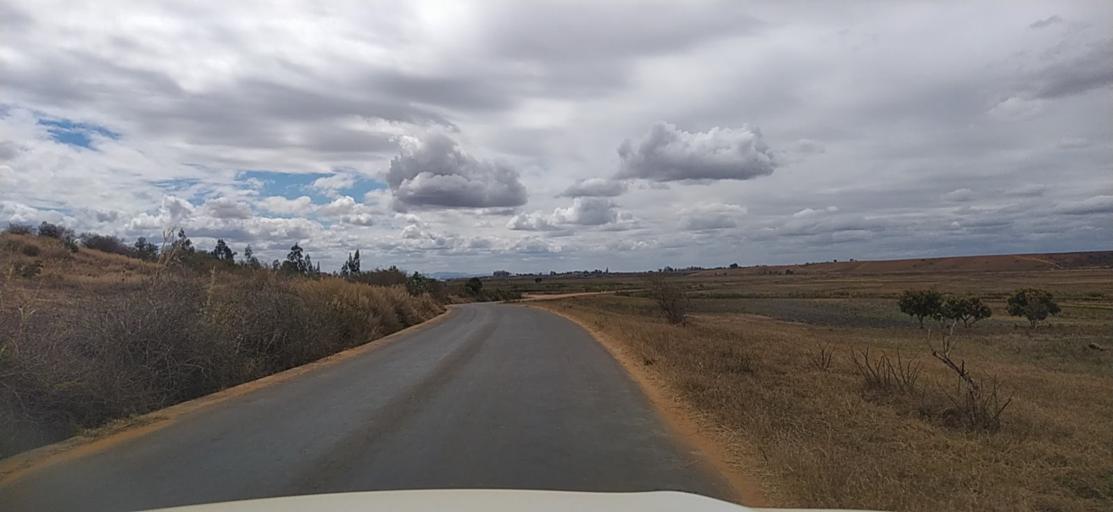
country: MG
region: Alaotra Mangoro
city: Ambatondrazaka
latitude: -17.9234
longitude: 48.2580
